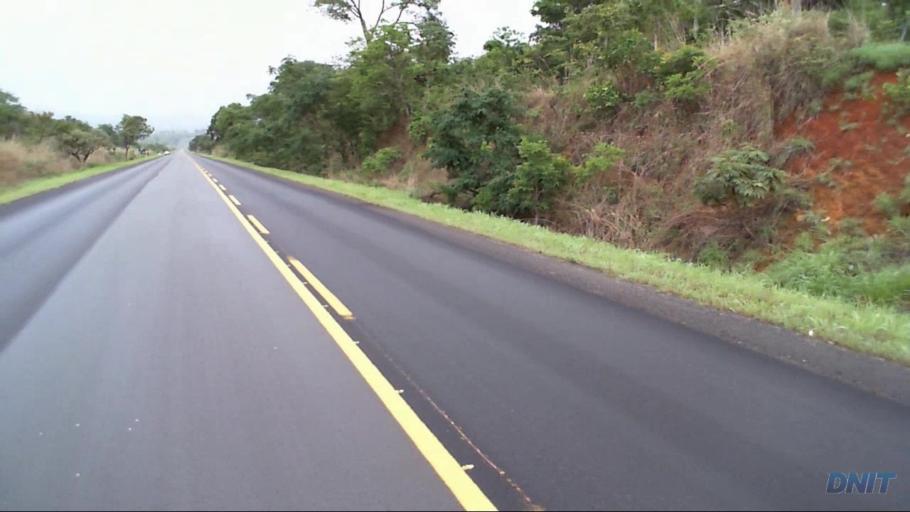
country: BR
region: Goias
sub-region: Padre Bernardo
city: Padre Bernardo
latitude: -15.2028
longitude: -48.4575
